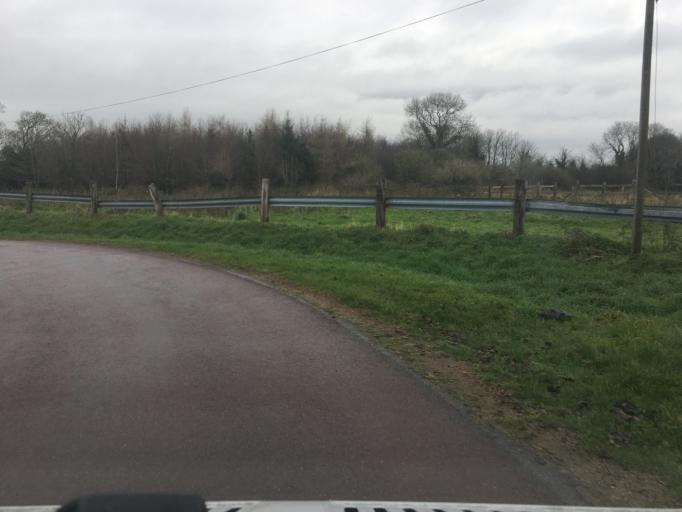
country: FR
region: Lower Normandy
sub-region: Departement de la Manche
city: Sainte-Mere-Eglise
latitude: 49.4257
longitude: -1.2643
